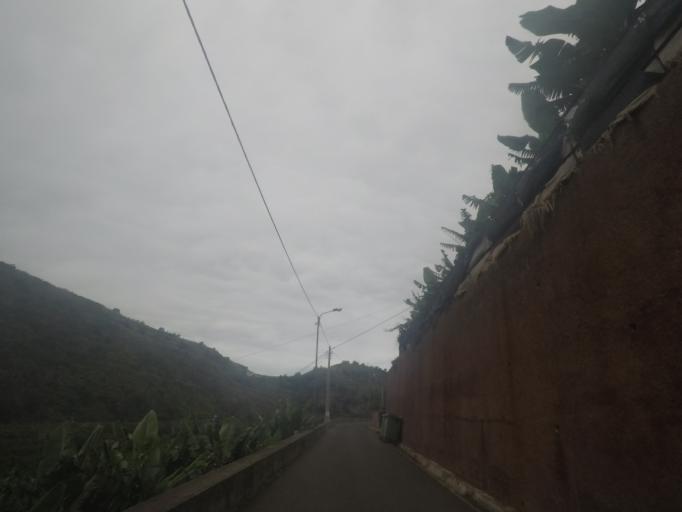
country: PT
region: Madeira
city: Camara de Lobos
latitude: 32.6661
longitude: -16.9615
